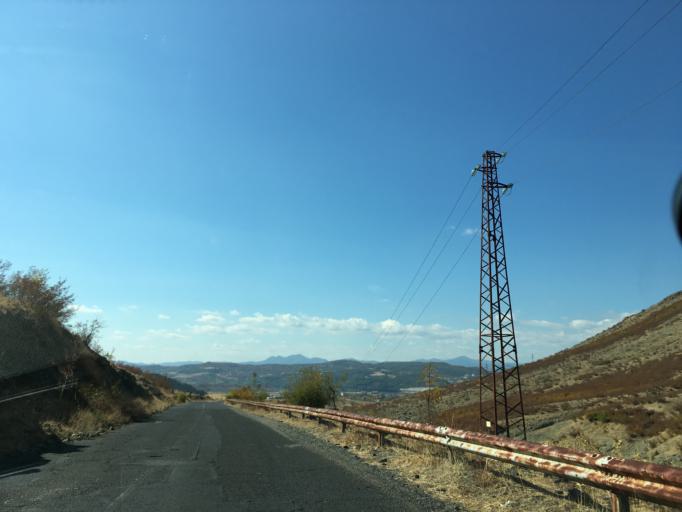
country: BG
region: Kurdzhali
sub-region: Obshtina Dzhebel
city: Dzhebel
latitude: 41.5239
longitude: 25.4386
